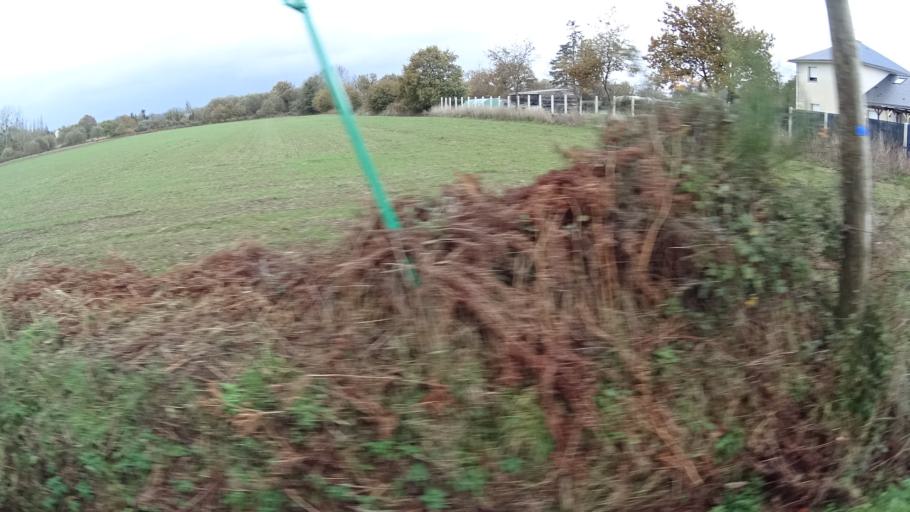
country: FR
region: Brittany
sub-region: Departement du Morbihan
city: Rieux
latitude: 47.5737
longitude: -2.1250
